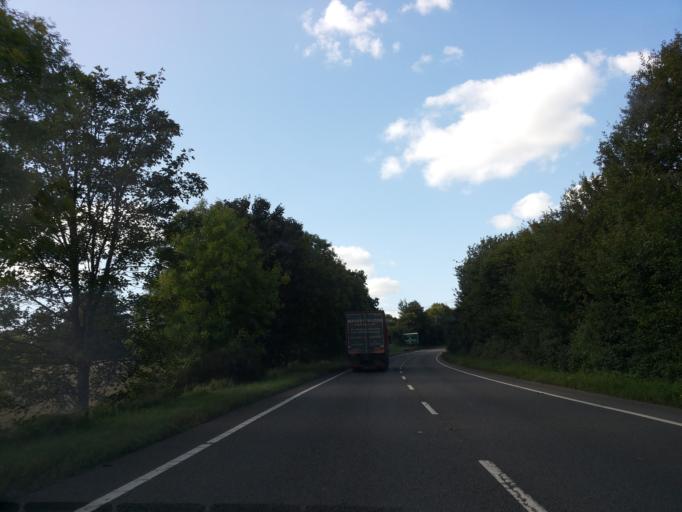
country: GB
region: England
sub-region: Wiltshire
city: Warminster
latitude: 51.1898
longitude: -2.1864
